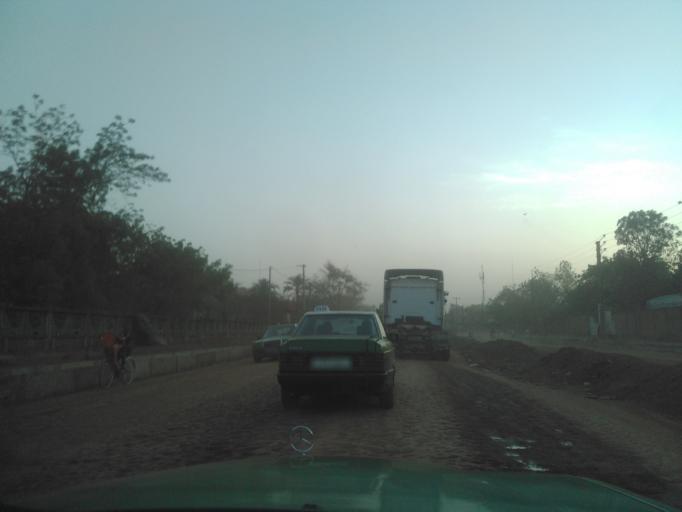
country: BF
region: Centre
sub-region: Kadiogo Province
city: Ouagadougou
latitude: 12.3815
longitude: -1.5070
